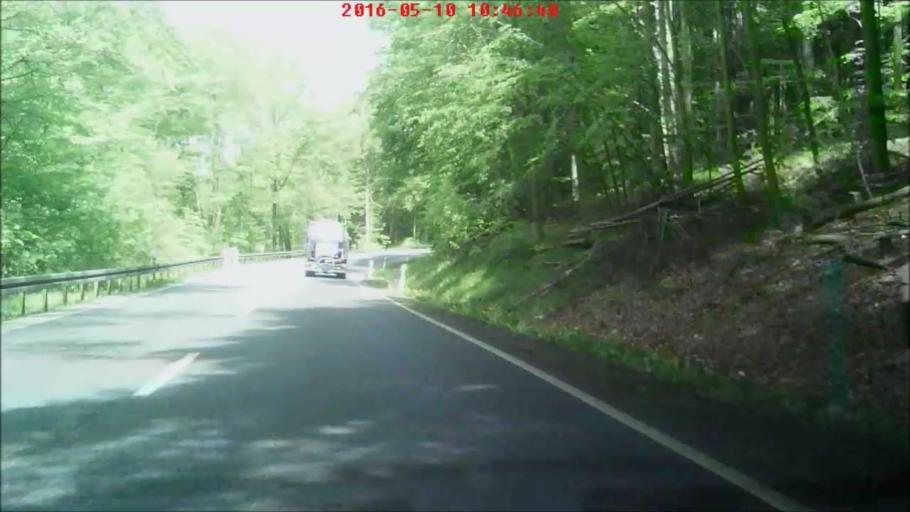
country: DE
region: Hesse
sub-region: Regierungsbezirk Kassel
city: Burghaun
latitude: 50.7437
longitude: 9.6883
